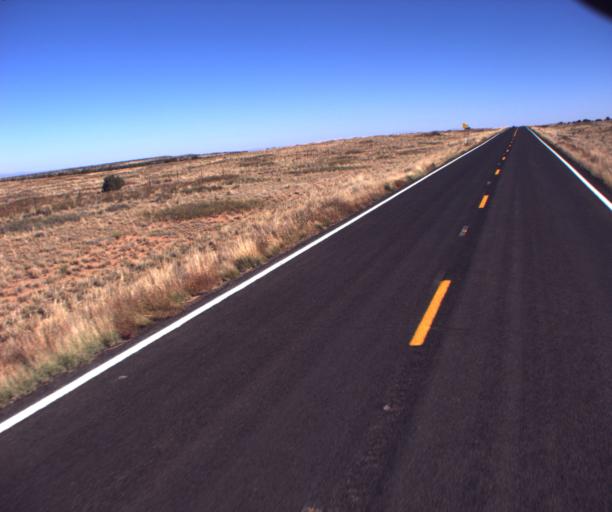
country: US
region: Arizona
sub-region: Coconino County
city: Tuba City
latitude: 35.9124
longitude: -110.8670
